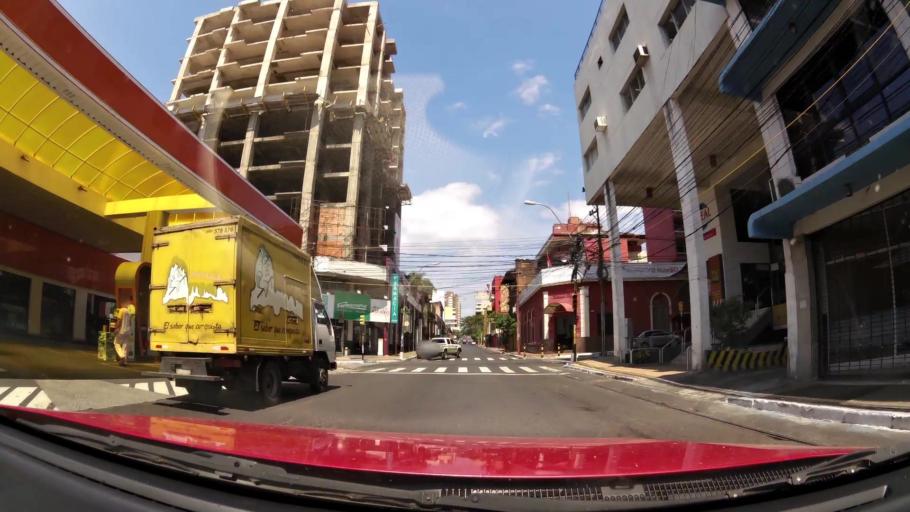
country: PY
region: Asuncion
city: Asuncion
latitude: -25.2862
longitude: -57.6289
